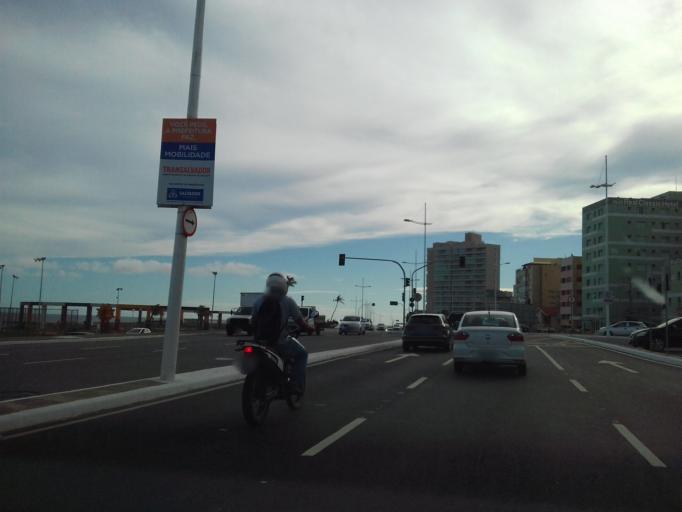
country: BR
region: Bahia
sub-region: Salvador
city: Salvador
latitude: -13.0015
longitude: -38.4507
